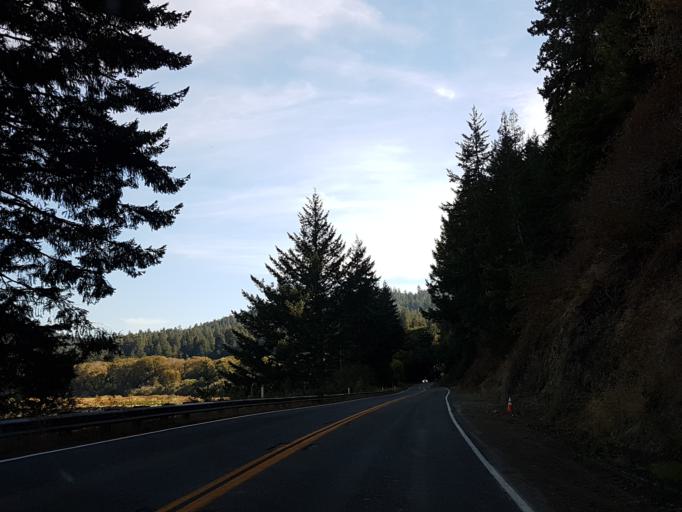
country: US
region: California
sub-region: Humboldt County
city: Rio Dell
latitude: 40.4254
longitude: -123.9803
